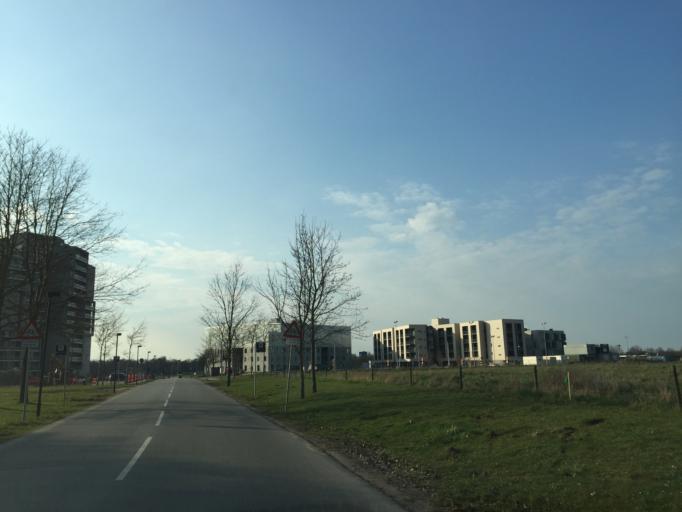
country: DK
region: South Denmark
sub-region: Odense Kommune
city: Neder Holluf
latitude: 55.3723
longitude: 10.4323
